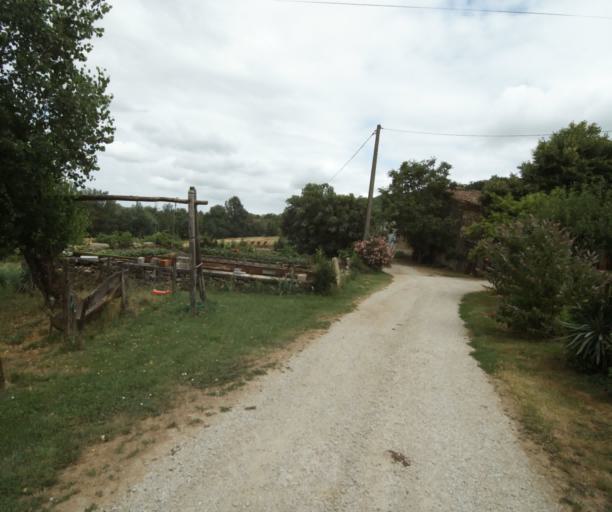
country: FR
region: Midi-Pyrenees
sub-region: Departement du Tarn
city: Soreze
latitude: 43.4546
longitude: 2.0805
